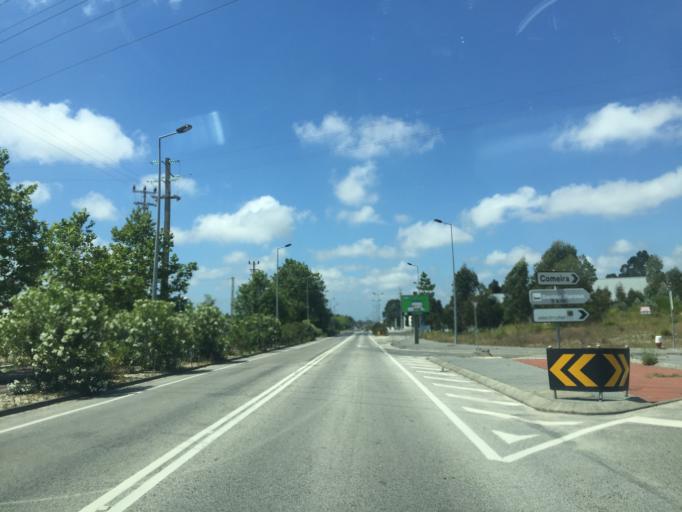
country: PT
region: Leiria
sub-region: Marinha Grande
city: Marinha Grande
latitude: 39.7216
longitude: -8.9265
